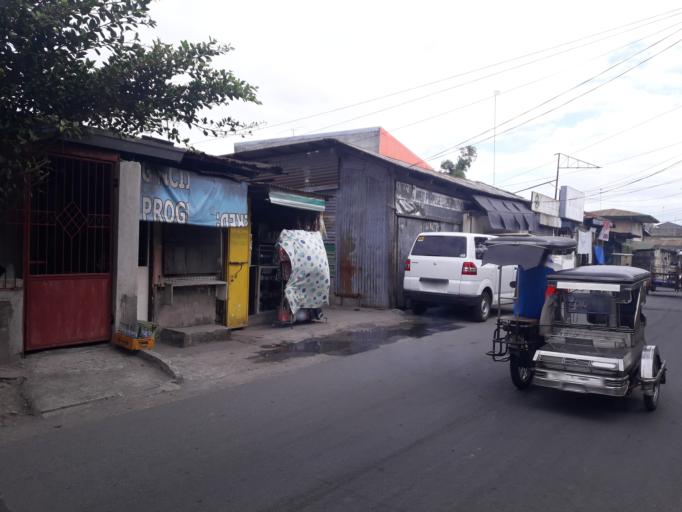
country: PH
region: Calabarzon
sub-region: Province of Laguna
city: Santa Rosa
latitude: 14.3069
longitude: 121.1242
